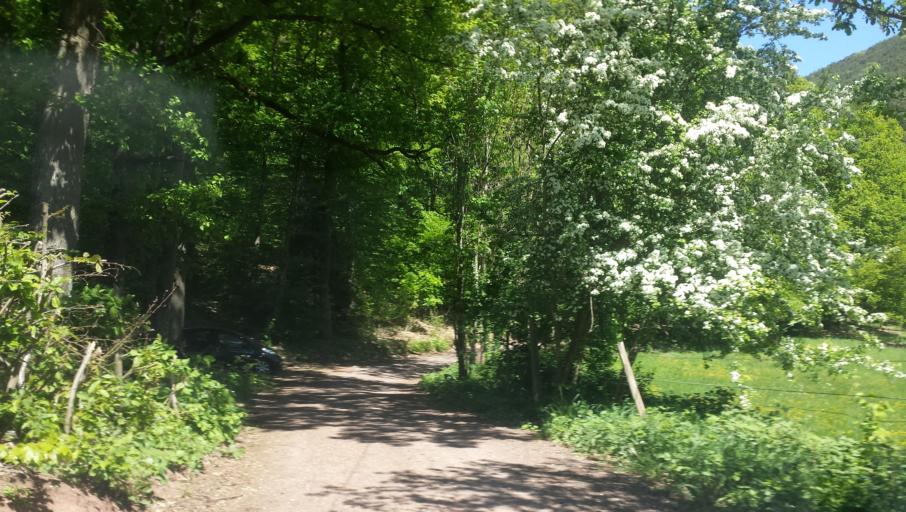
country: DE
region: Rheinland-Pfalz
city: Ramberg
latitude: 49.2711
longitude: 8.0447
